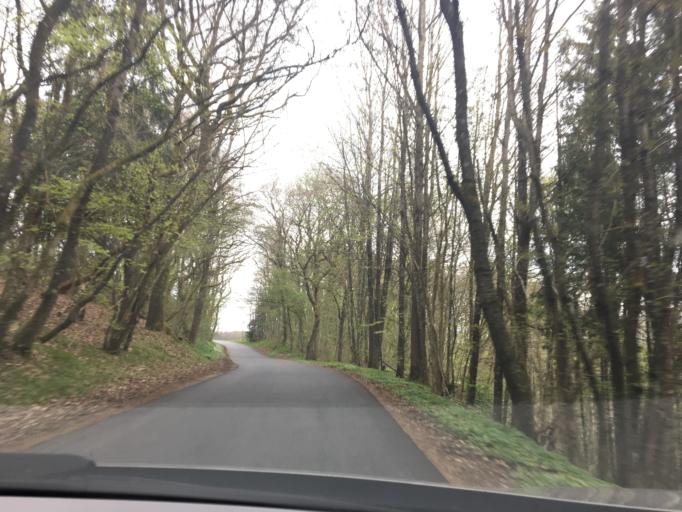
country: DK
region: Central Jutland
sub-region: Horsens Kommune
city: Braedstrup
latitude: 55.9599
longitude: 9.6887
